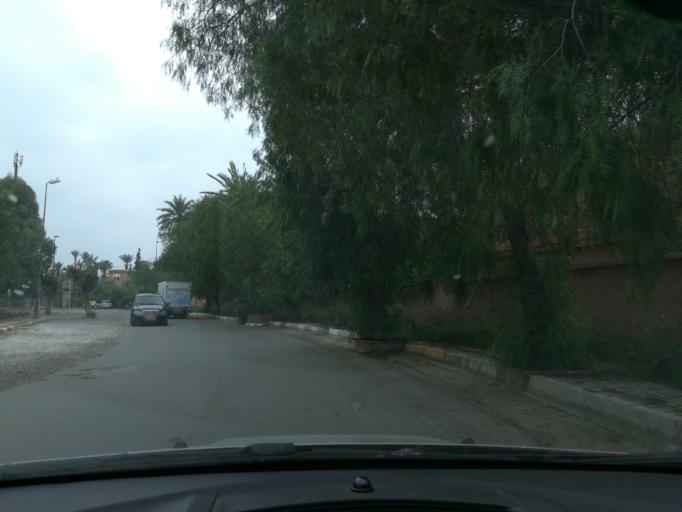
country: MA
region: Marrakech-Tensift-Al Haouz
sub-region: Marrakech
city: Marrakesh
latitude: 31.6824
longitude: -7.9850
